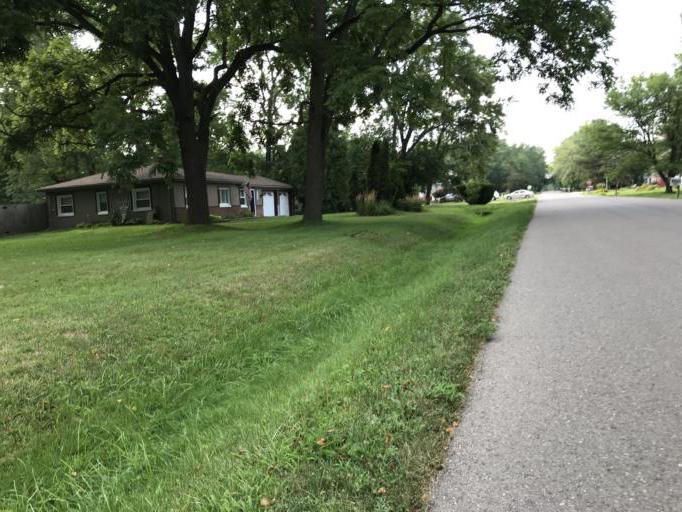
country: US
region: Michigan
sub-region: Oakland County
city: Farmington
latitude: 42.4645
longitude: -83.3485
